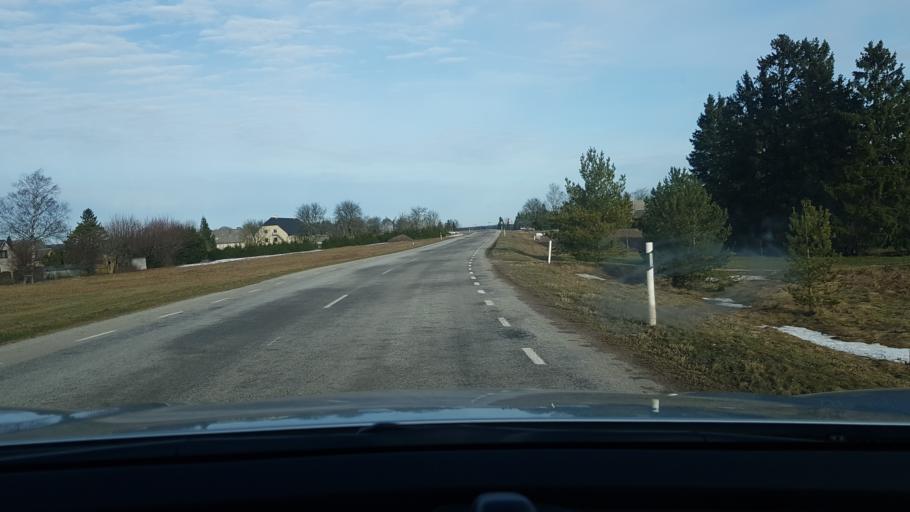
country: EE
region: Saare
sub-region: Kuressaare linn
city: Kuressaare
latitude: 58.5230
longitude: 22.7015
